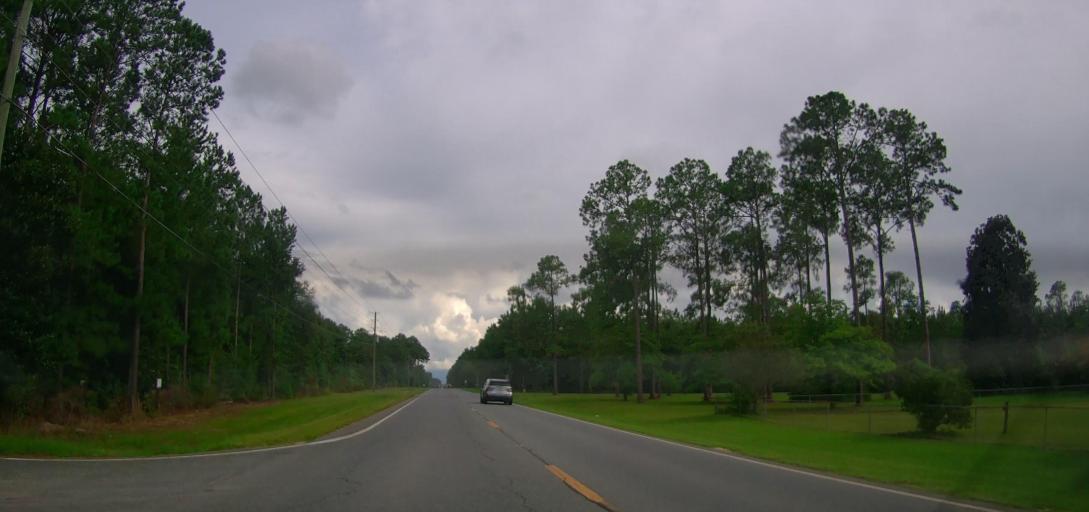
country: US
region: Georgia
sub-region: Wayne County
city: Jesup
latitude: 31.6533
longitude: -81.9111
